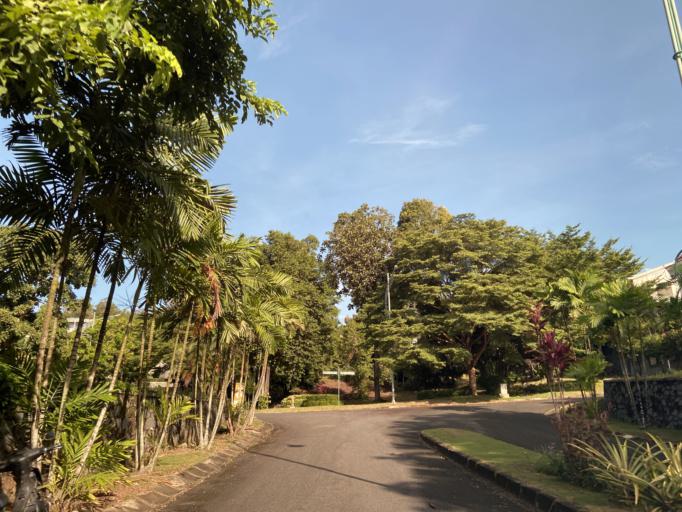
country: SG
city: Singapore
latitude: 1.0976
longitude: 104.0300
